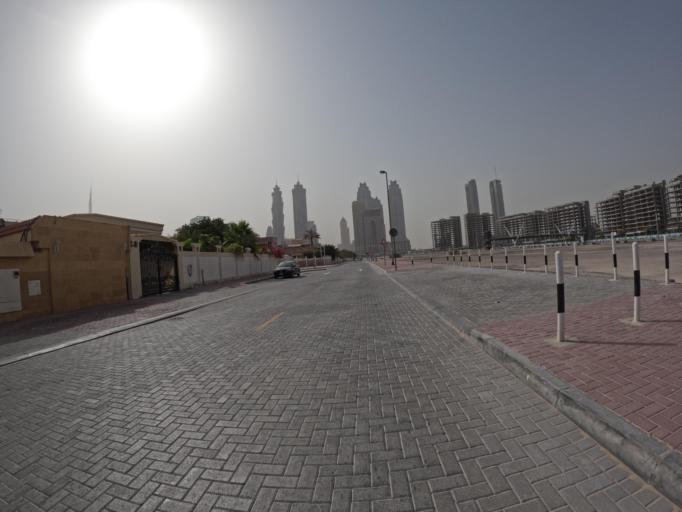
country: AE
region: Dubai
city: Dubai
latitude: 25.1892
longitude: 55.2468
